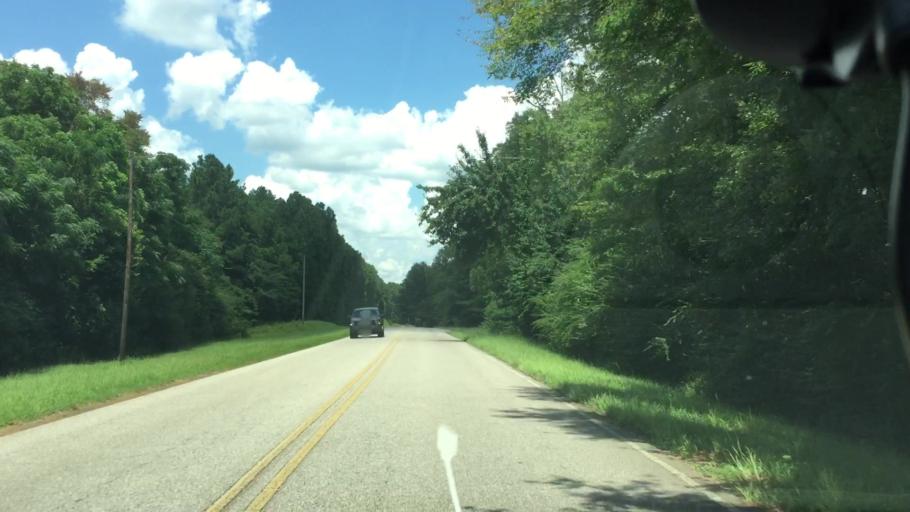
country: US
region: Alabama
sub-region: Pike County
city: Troy
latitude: 31.7636
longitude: -85.9826
